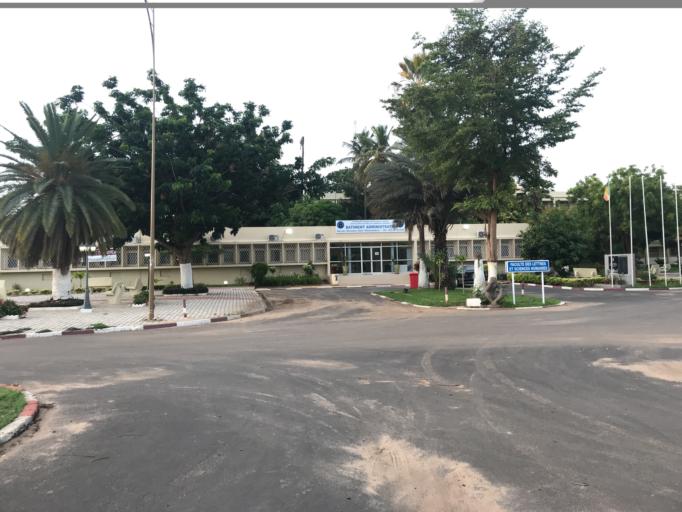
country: SN
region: Dakar
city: Dakar
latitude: 14.6855
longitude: -17.4640
